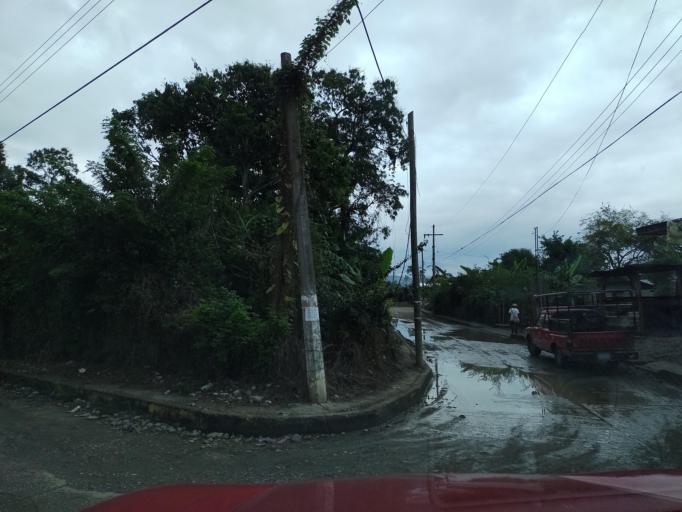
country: MX
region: Veracruz
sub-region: Papantla
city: El Chote
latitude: 20.4291
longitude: -97.3847
